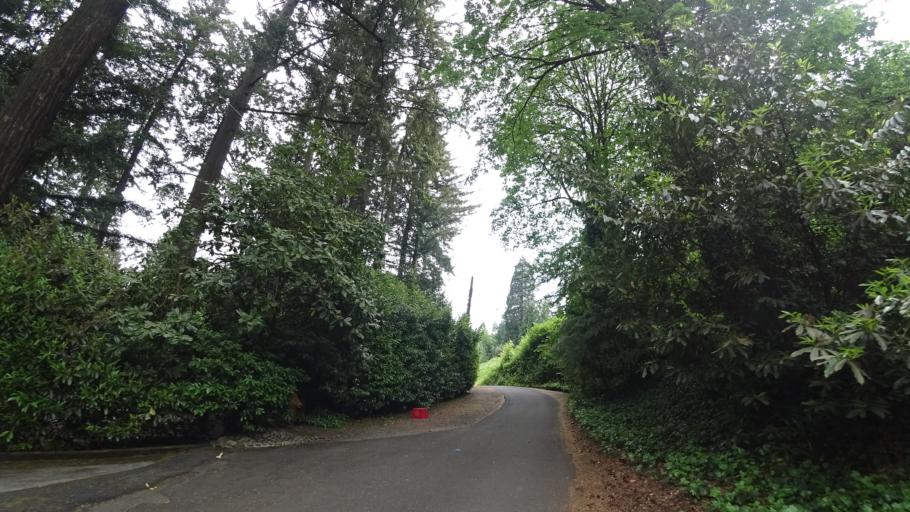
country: US
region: Oregon
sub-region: Clackamas County
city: Milwaukie
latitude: 45.4469
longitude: -122.6605
